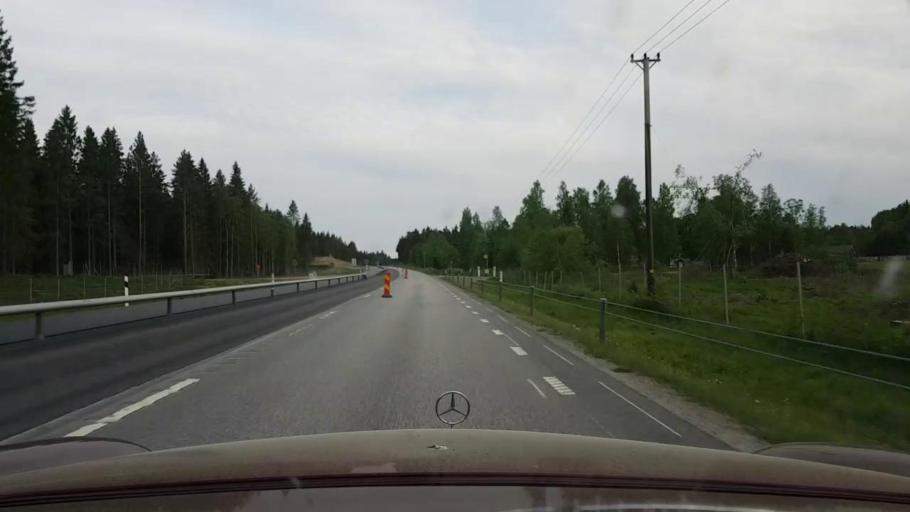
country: SE
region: OErebro
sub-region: Askersunds Kommun
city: Asbro
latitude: 58.9608
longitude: 15.0334
